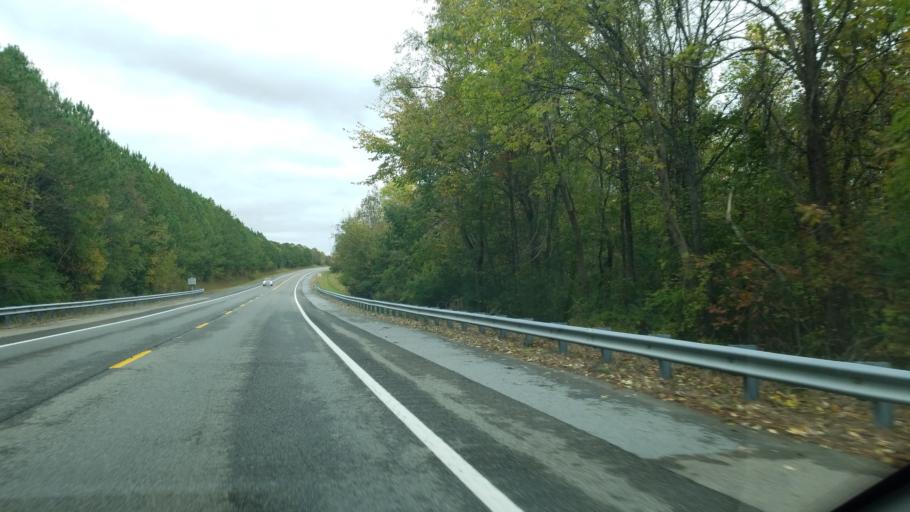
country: US
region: Tennessee
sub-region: Rhea County
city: Graysville
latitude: 35.4145
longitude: -85.0220
